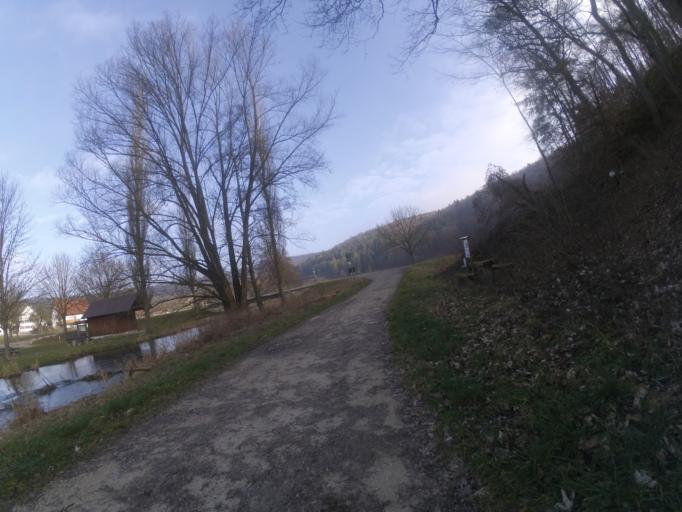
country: DE
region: Baden-Wuerttemberg
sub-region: Tuebingen Region
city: Rechtenstein
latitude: 48.2647
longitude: 9.5413
